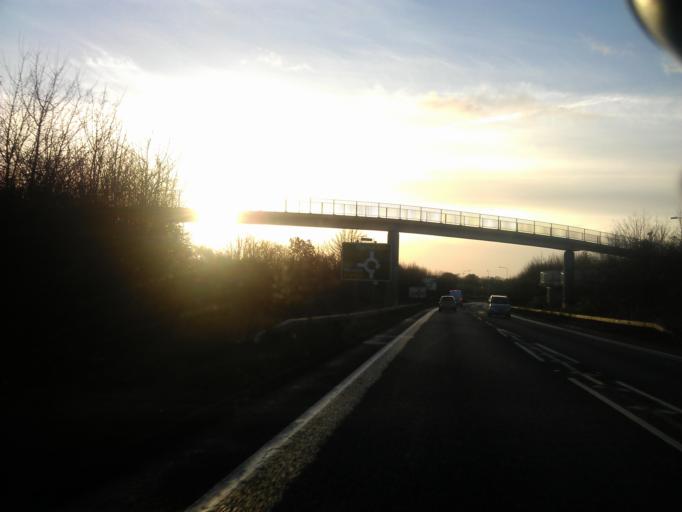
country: GB
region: England
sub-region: Essex
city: Little Clacton
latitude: 51.8221
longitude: 1.1349
